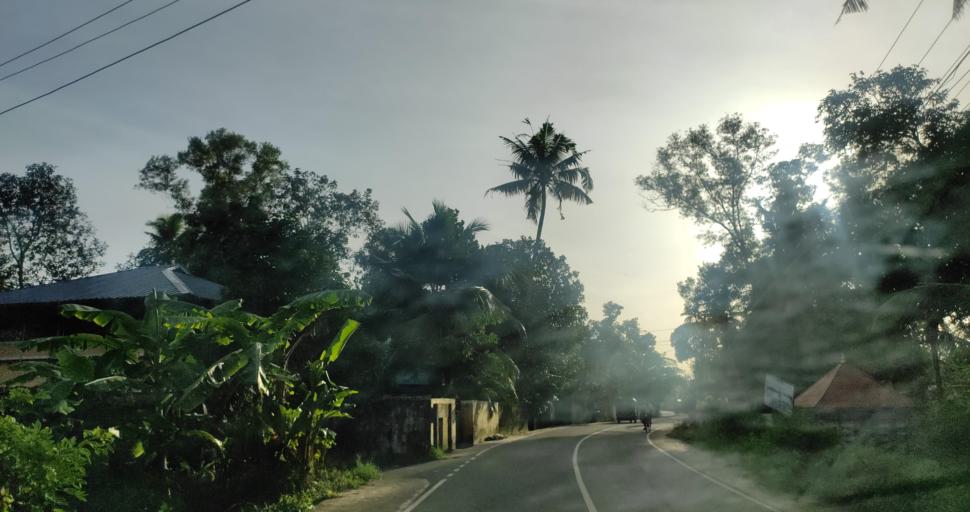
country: IN
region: Kerala
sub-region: Alappuzha
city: Shertallai
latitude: 9.6018
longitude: 76.3062
